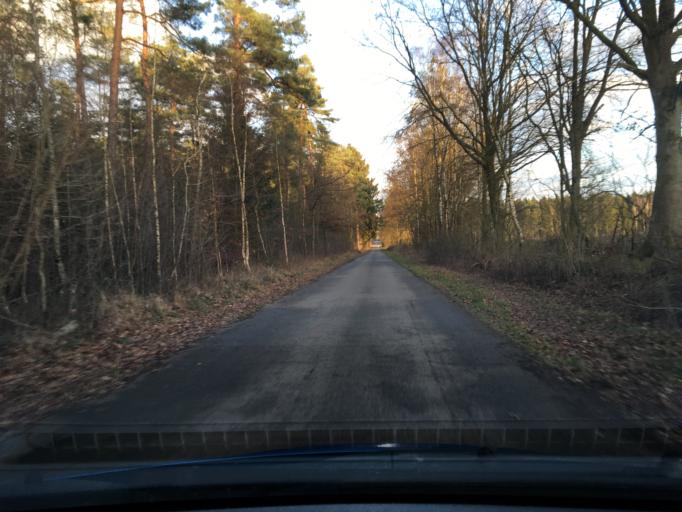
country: DE
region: Lower Saxony
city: Soderstorf
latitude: 53.1078
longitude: 10.1410
